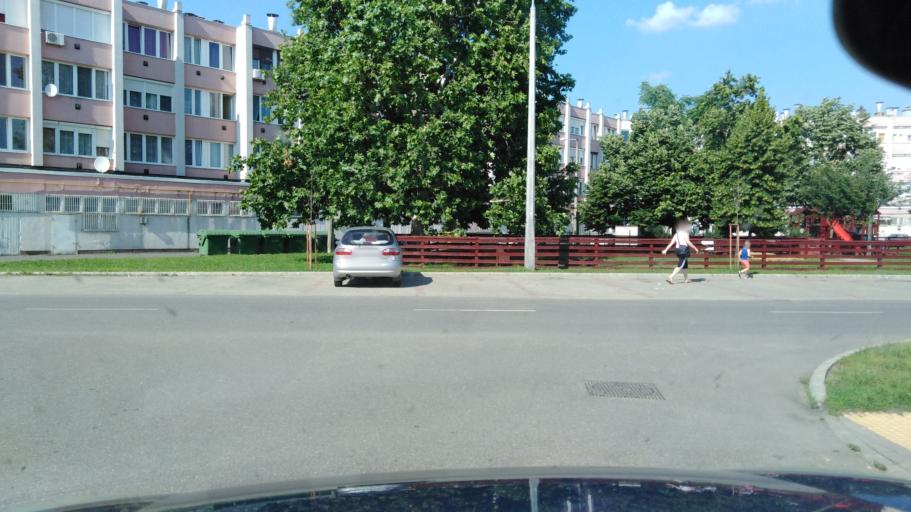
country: HU
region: Szabolcs-Szatmar-Bereg
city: Nyirbator
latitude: 47.8348
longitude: 22.1306
